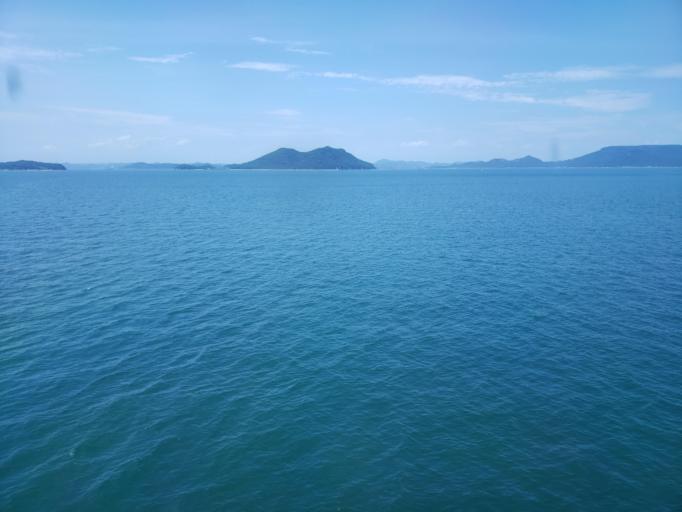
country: JP
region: Kagawa
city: Takamatsu-shi
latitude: 34.3925
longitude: 134.0963
